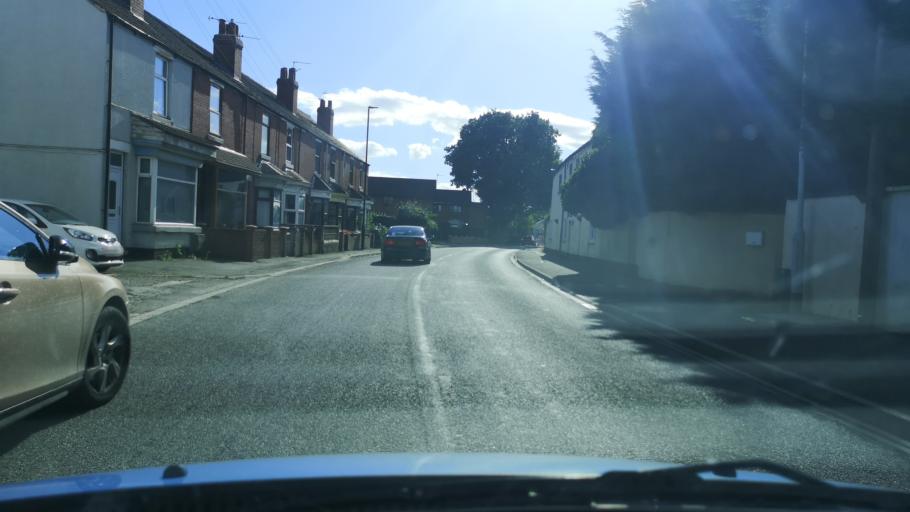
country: GB
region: England
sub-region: Doncaster
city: Doncaster
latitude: 53.5579
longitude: -1.1220
